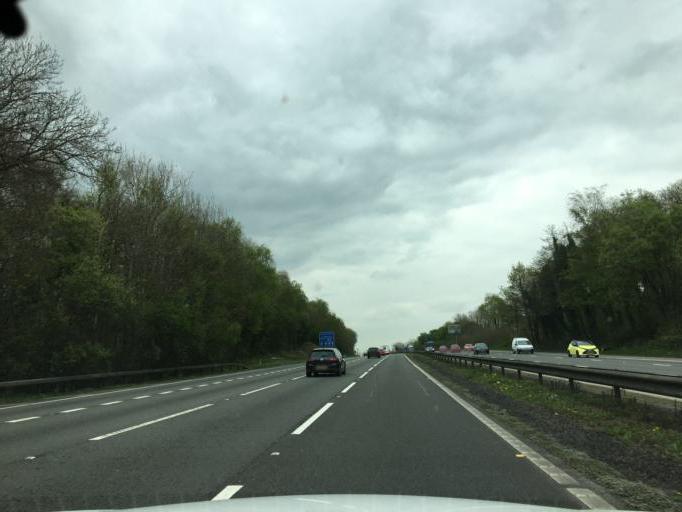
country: GB
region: Wales
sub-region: Cardiff
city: Pentyrch
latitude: 51.5074
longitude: -3.3264
